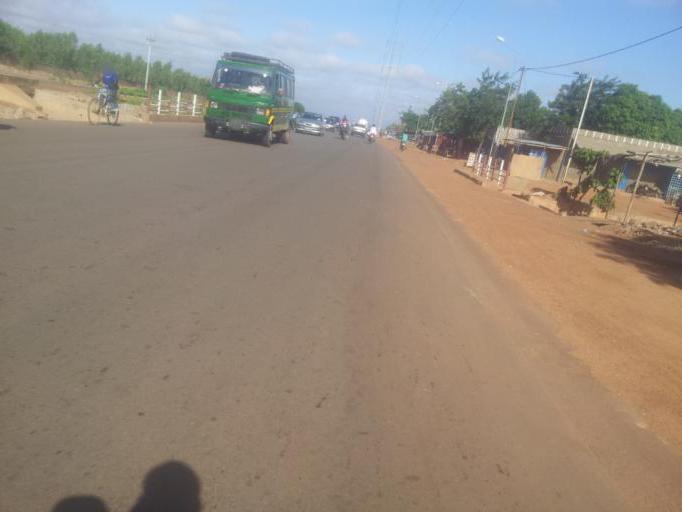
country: BF
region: Centre
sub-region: Kadiogo Province
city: Ouagadougou
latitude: 12.3700
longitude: -1.5609
